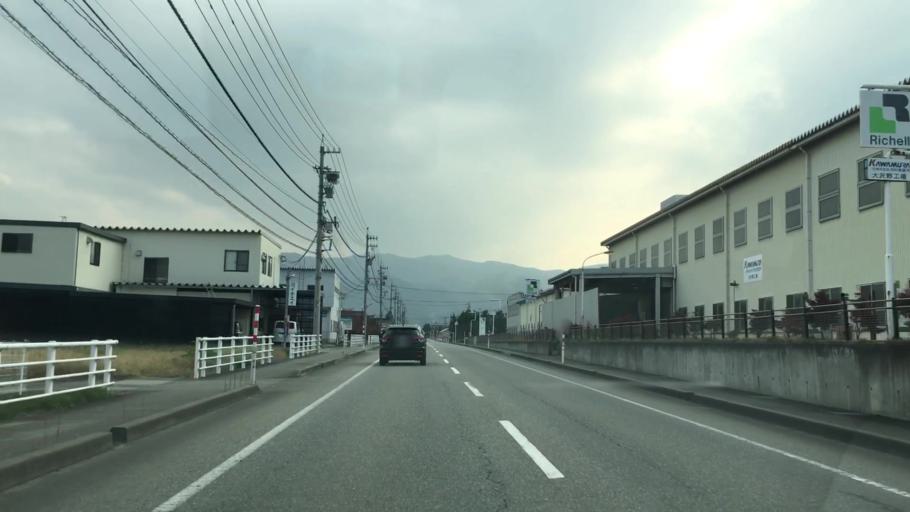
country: JP
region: Toyama
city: Yatsuomachi-higashikumisaka
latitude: 36.5891
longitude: 137.1906
